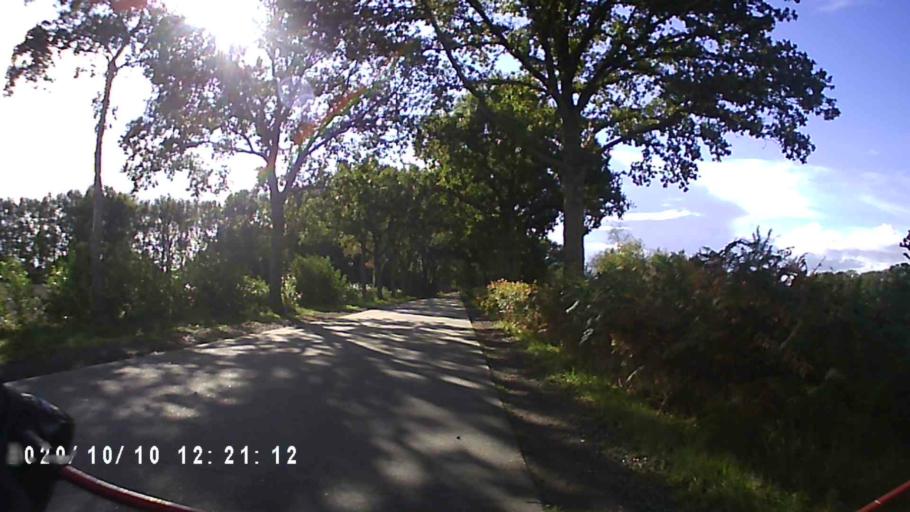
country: NL
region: Friesland
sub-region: Gemeente Heerenveen
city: Jubbega
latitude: 53.0057
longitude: 6.1806
